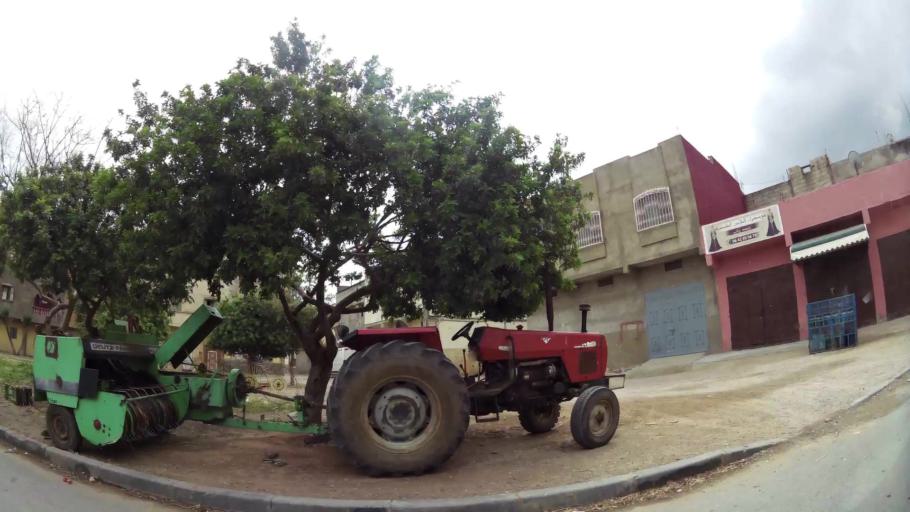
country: MA
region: Rabat-Sale-Zemmour-Zaer
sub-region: Khemisset
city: Tiflet
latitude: 33.8894
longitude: -6.3221
